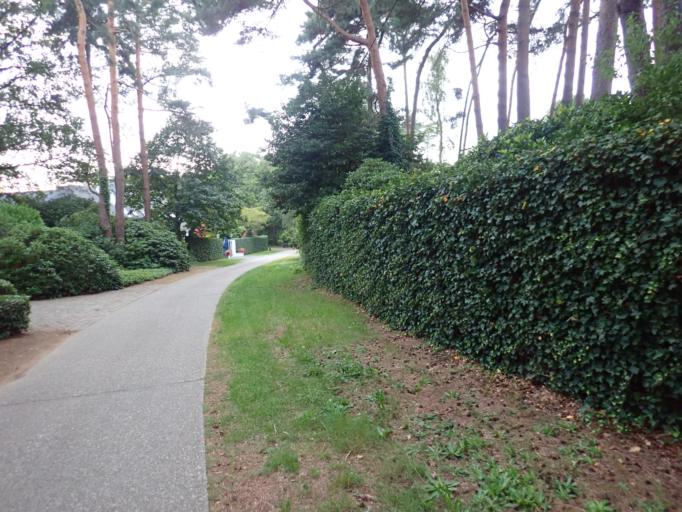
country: BE
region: Flanders
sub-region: Provincie Antwerpen
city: Schilde
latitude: 51.2261
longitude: 4.5560
